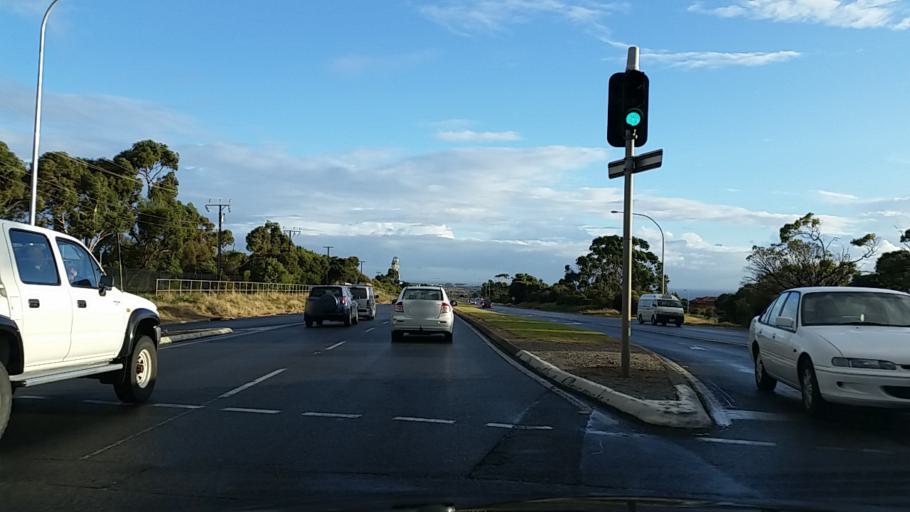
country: AU
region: South Australia
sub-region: Marion
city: Happy Valley
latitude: -35.0721
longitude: 138.5255
